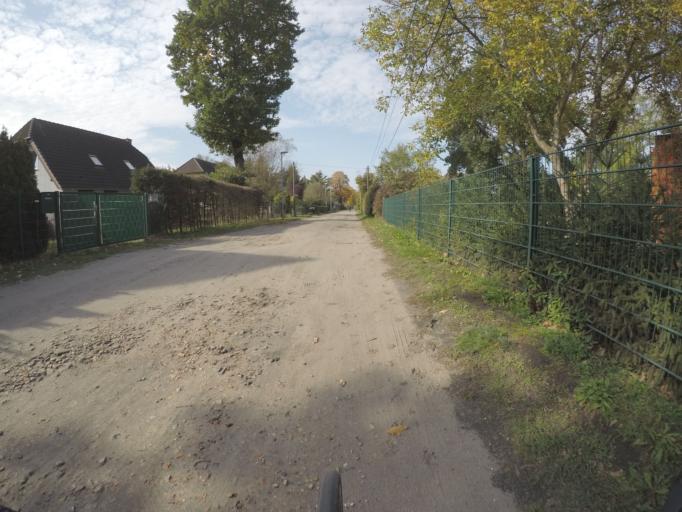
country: DE
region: Brandenburg
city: Leegebruch
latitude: 52.7451
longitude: 13.2078
